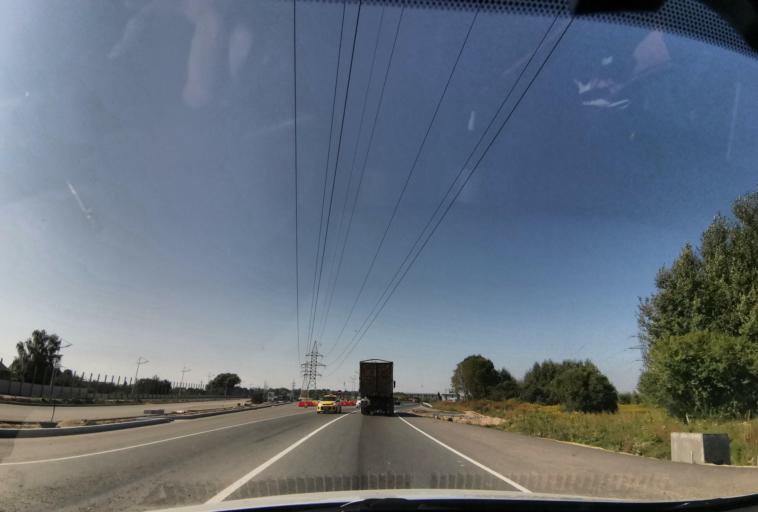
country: RU
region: Kaliningrad
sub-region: Gorod Kaliningrad
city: Kaliningrad
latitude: 54.7706
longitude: 20.5018
